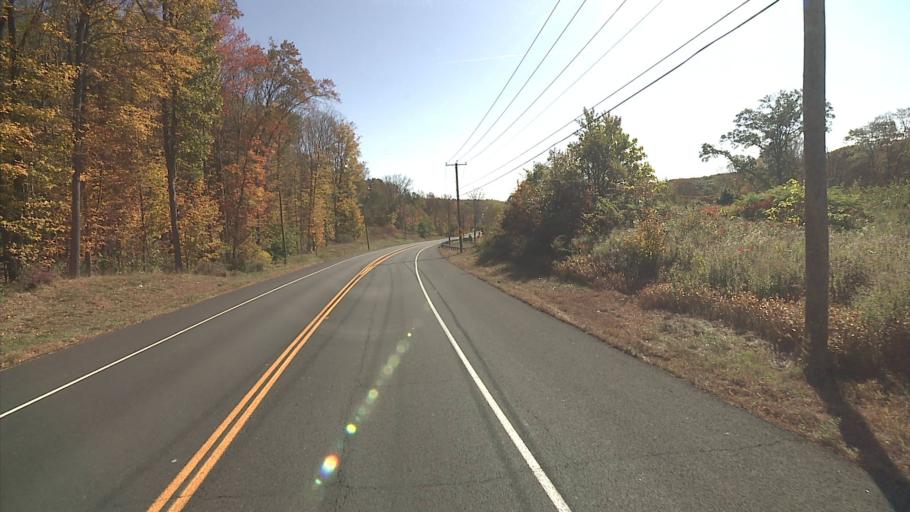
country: US
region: Connecticut
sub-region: Tolland County
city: Rockville
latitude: 41.7826
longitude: -72.4253
